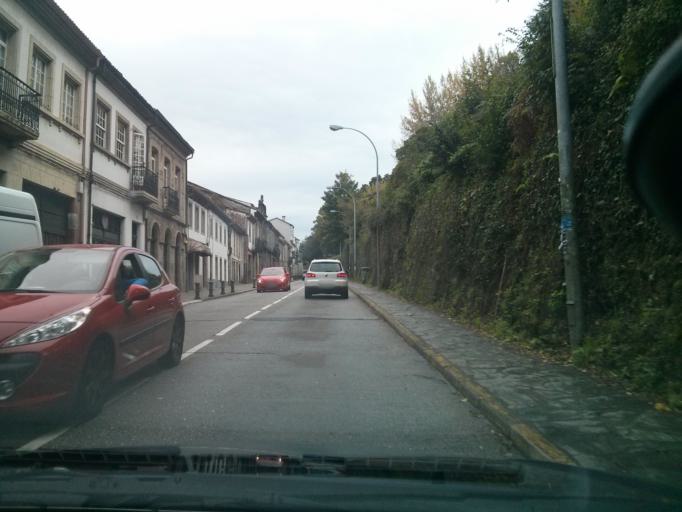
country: ES
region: Galicia
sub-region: Provincia da Coruna
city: Santiago de Compostela
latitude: 42.8795
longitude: -8.5491
